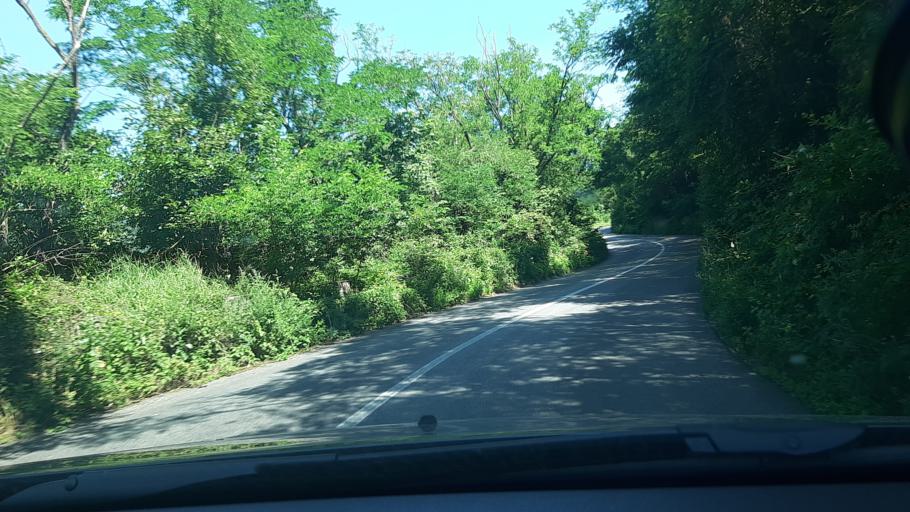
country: RO
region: Hunedoara
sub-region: Comuna Teliucu Inferior
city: Teliucu Inferior
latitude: 45.7009
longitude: 22.8776
